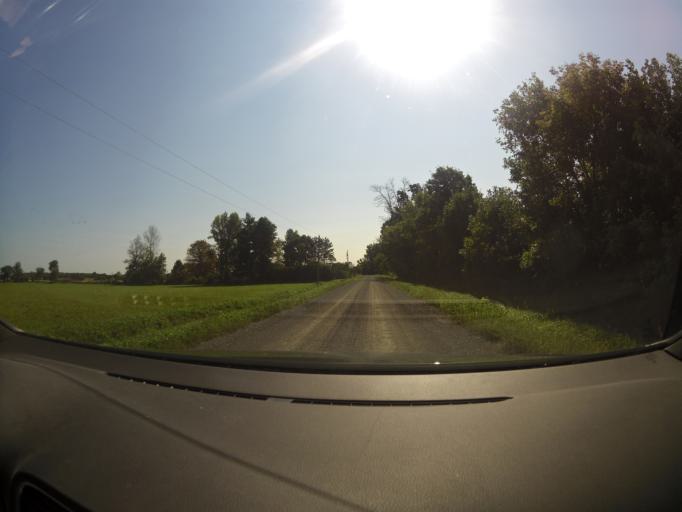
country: CA
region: Ontario
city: Arnprior
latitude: 45.3549
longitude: -76.2847
